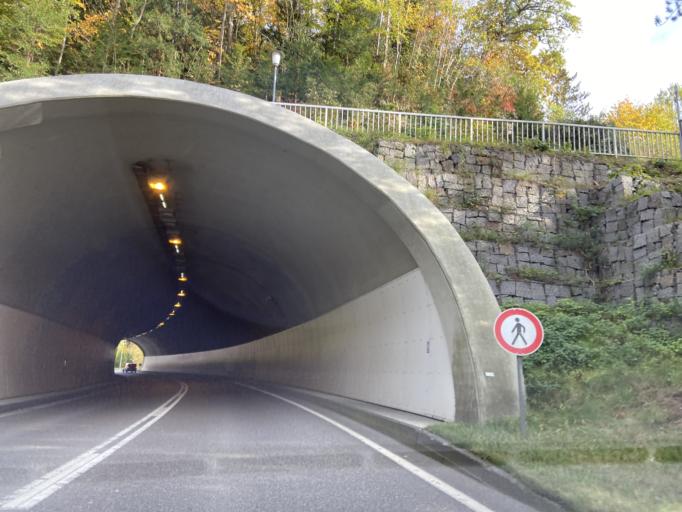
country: DE
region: Baden-Wuerttemberg
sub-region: Tuebingen Region
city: Sigmaringen
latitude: 48.0896
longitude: 9.2156
